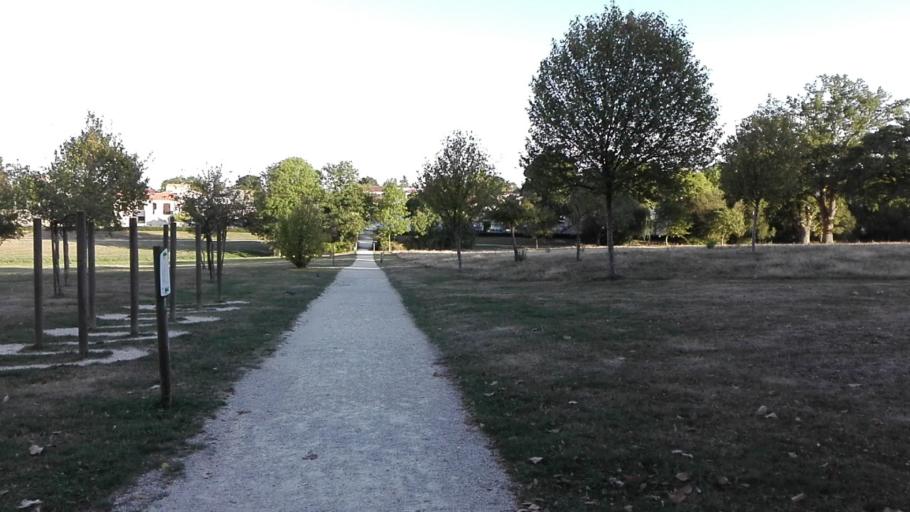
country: FR
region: Pays de la Loire
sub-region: Departement de la Vendee
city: Les Essarts
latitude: 46.7720
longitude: -1.2304
